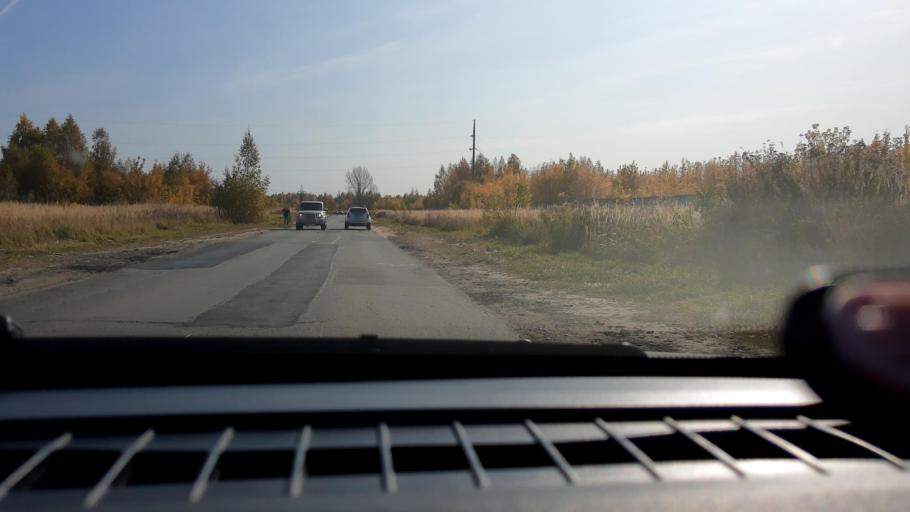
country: RU
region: Nizjnij Novgorod
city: Kstovo
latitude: 56.1496
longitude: 44.2244
